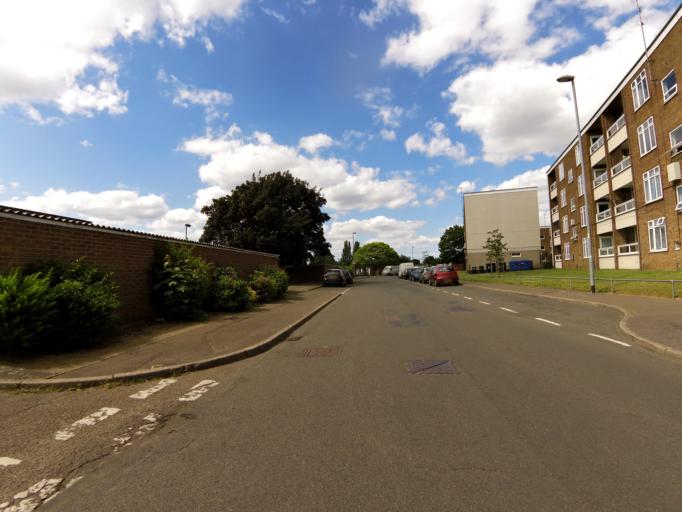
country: GB
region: England
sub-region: Norfolk
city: Norwich
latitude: 52.6526
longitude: 1.2695
